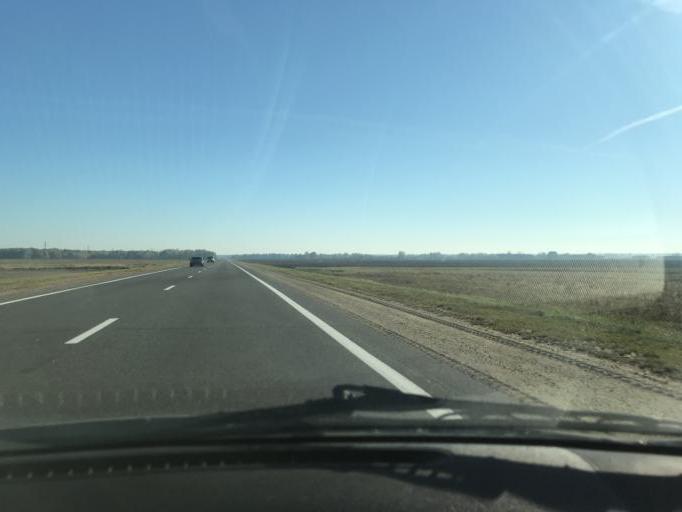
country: BY
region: Brest
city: Ivanava
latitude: 52.1560
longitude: 25.6746
